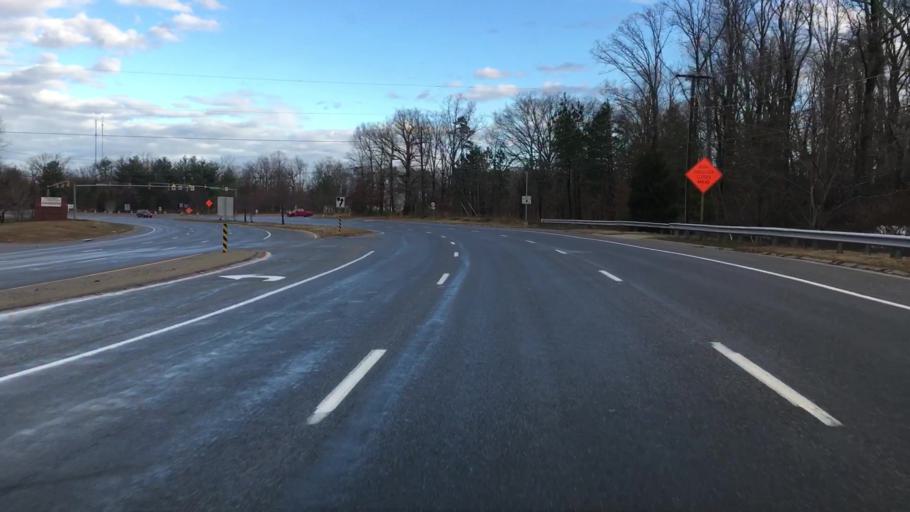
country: US
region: Virginia
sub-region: Chesterfield County
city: Bon Air
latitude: 37.4887
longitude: -77.5964
